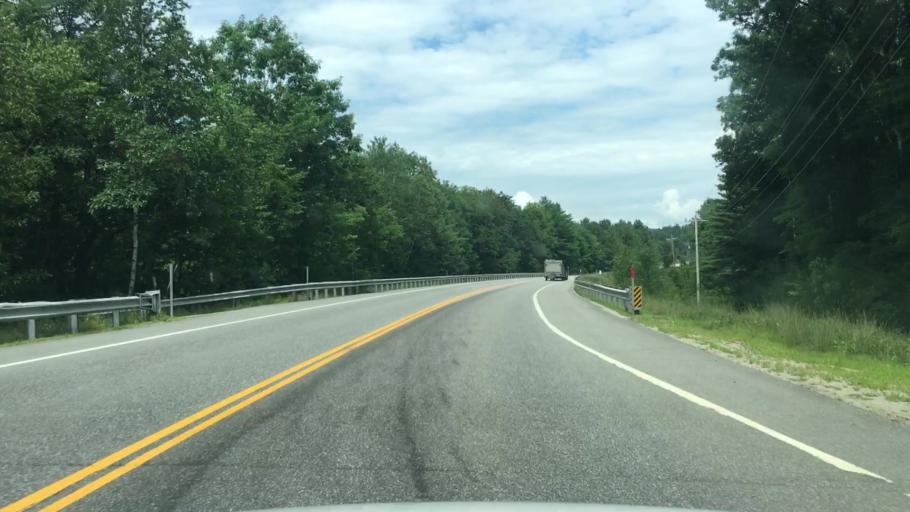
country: US
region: New Hampshire
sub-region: Grafton County
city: Rumney
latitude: 43.8481
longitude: -71.9113
